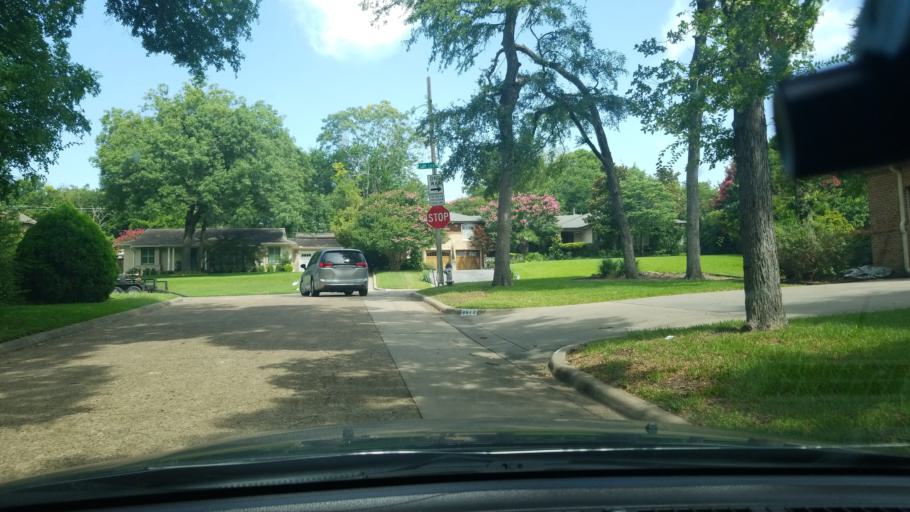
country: US
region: Texas
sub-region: Dallas County
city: Highland Park
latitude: 32.8154
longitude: -96.7082
